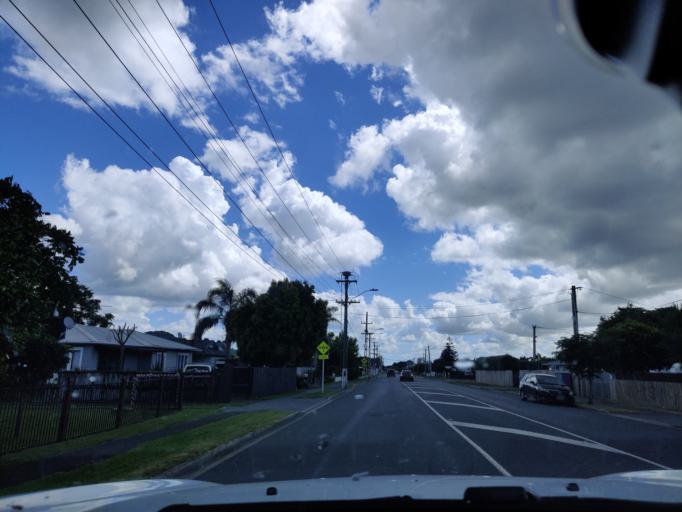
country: NZ
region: Auckland
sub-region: Auckland
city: Red Hill
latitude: -37.0545
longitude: 174.9595
